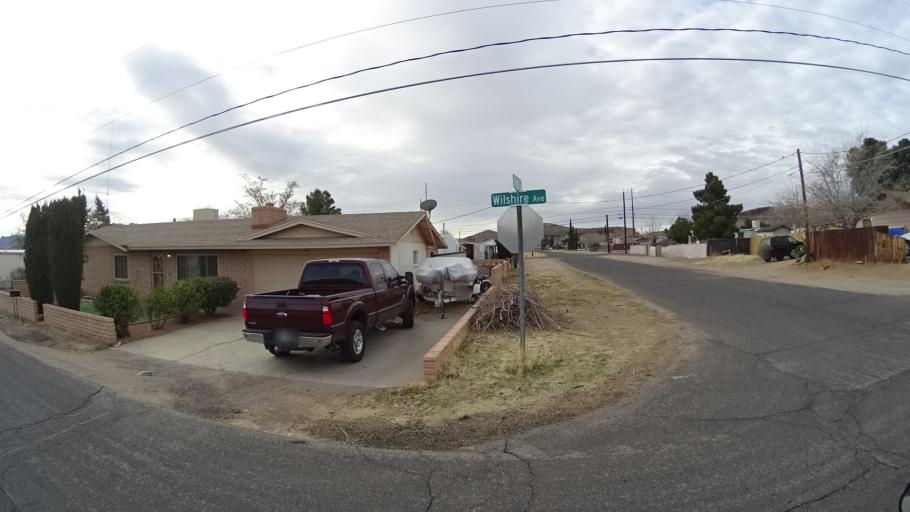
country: US
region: Arizona
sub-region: Mohave County
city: Kingman
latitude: 35.2185
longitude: -114.0510
